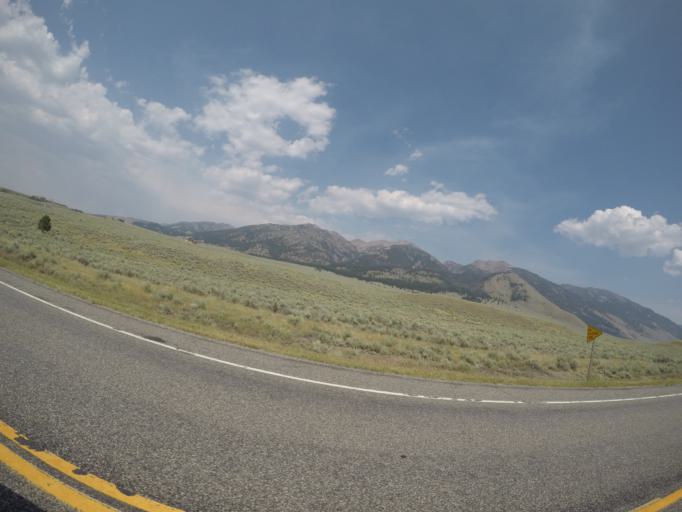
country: US
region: Montana
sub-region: Gallatin County
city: Big Sky
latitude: 44.8497
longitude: -111.5332
